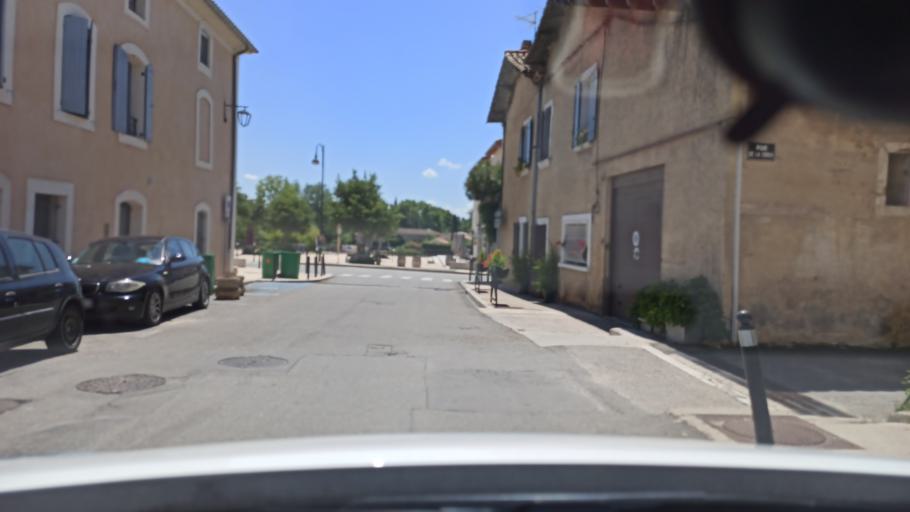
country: FR
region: Provence-Alpes-Cote d'Azur
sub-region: Departement du Vaucluse
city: Caumont-sur-Durance
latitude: 43.8933
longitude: 4.9441
